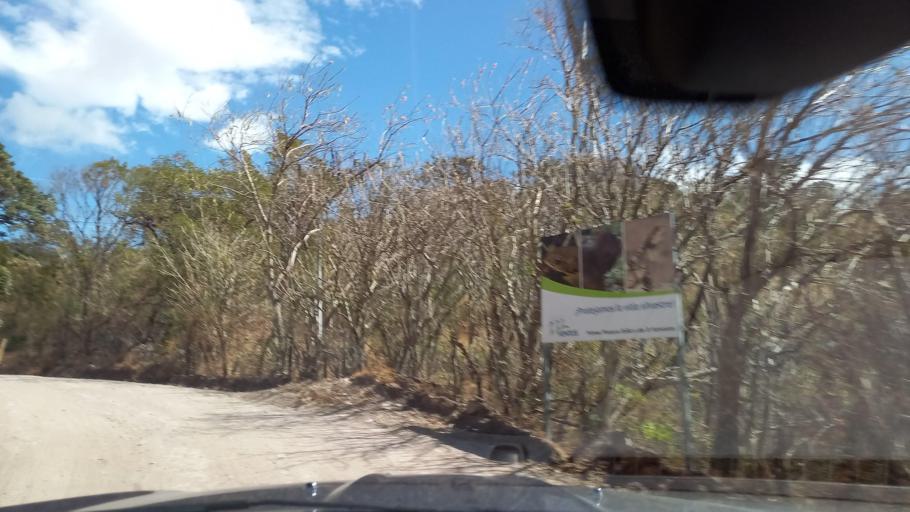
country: SV
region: Santa Ana
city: Metapan
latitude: 14.3676
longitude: -89.4958
